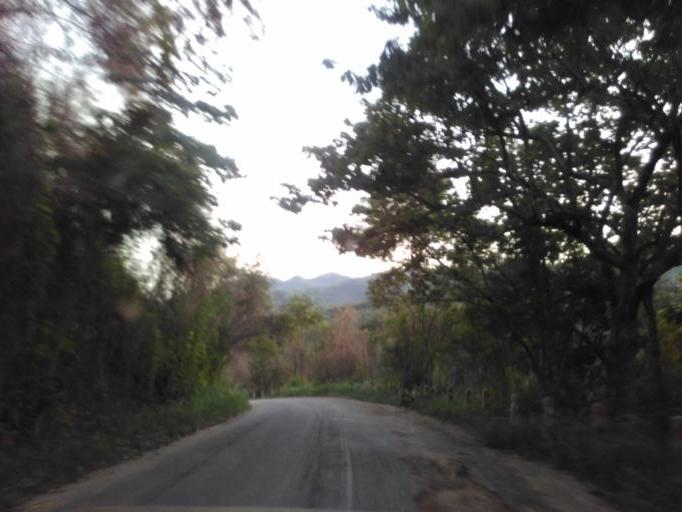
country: GH
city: Bekwai
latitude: 6.5408
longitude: -1.4323
